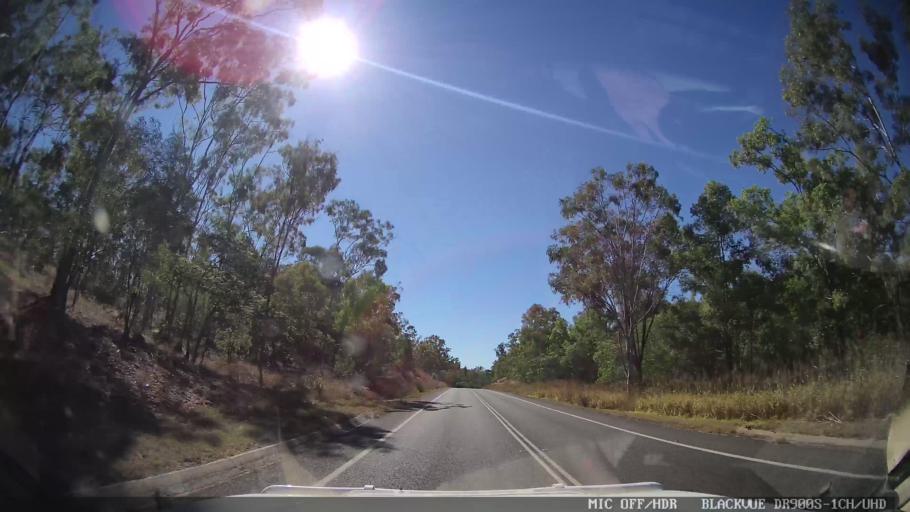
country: AU
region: Queensland
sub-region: Gladstone
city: Toolooa
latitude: -23.9658
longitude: 151.2175
